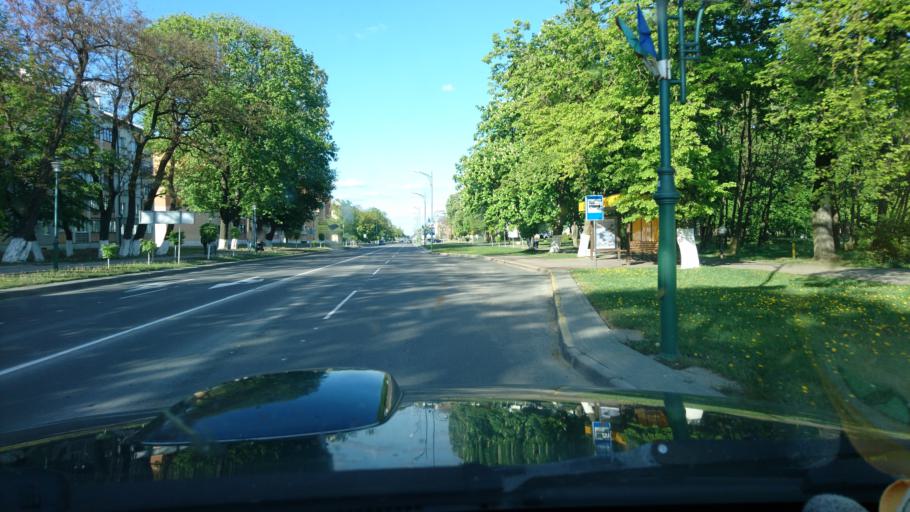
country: BY
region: Brest
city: Byaroza
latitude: 52.5240
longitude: 24.9641
